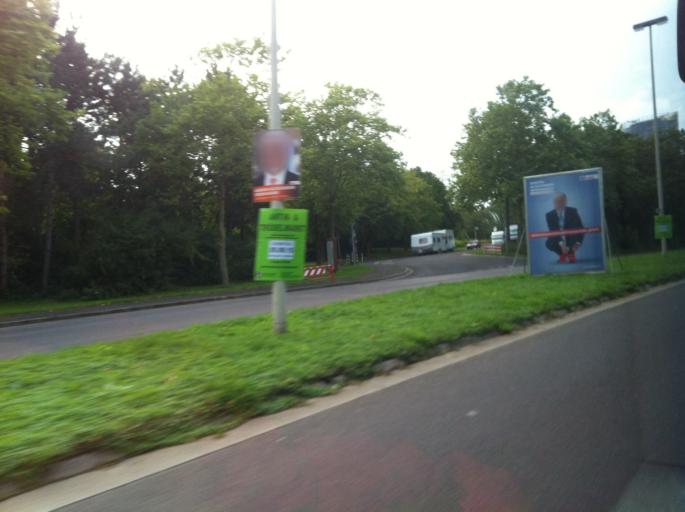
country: DE
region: North Rhine-Westphalia
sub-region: Regierungsbezirk Koln
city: Bonn
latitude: 50.7091
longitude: 7.1408
